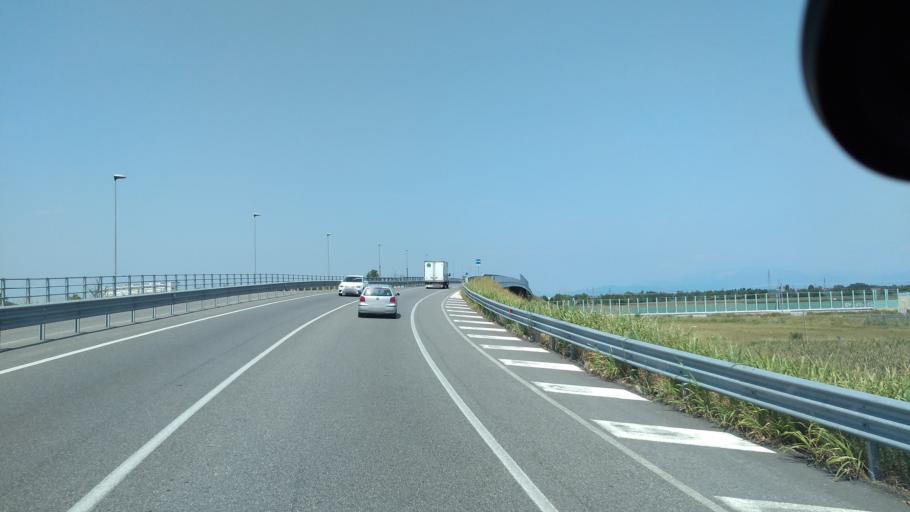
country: IT
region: Lombardy
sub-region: Provincia di Bergamo
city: Caravaggio
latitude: 45.5054
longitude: 9.6206
